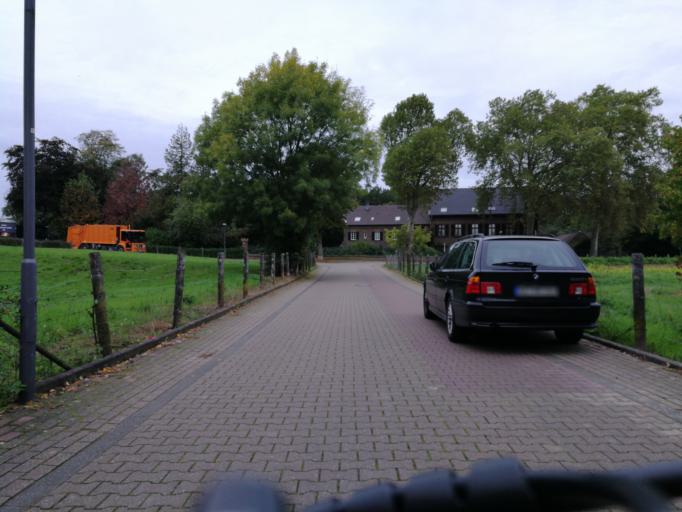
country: DE
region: North Rhine-Westphalia
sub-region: Regierungsbezirk Dusseldorf
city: Dusseldorf
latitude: 51.1484
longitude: 6.7529
